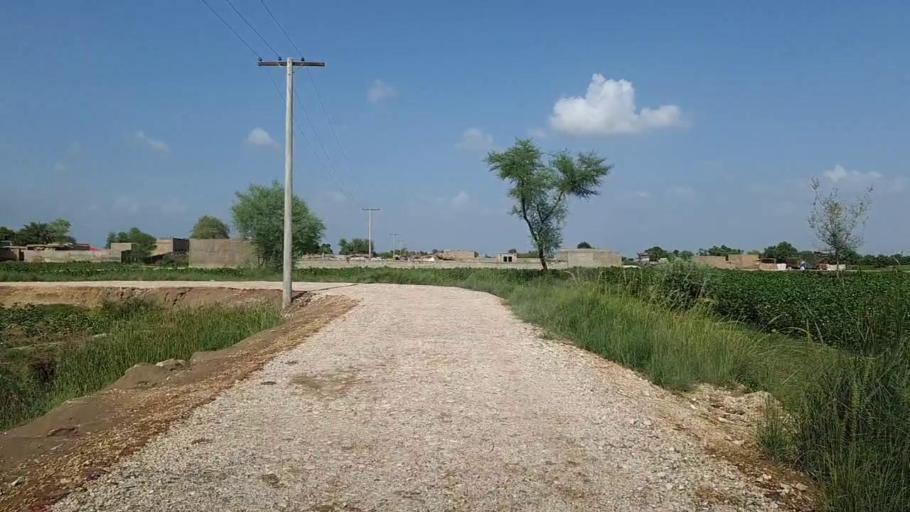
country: PK
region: Sindh
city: Bhiria
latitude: 26.8700
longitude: 68.2367
